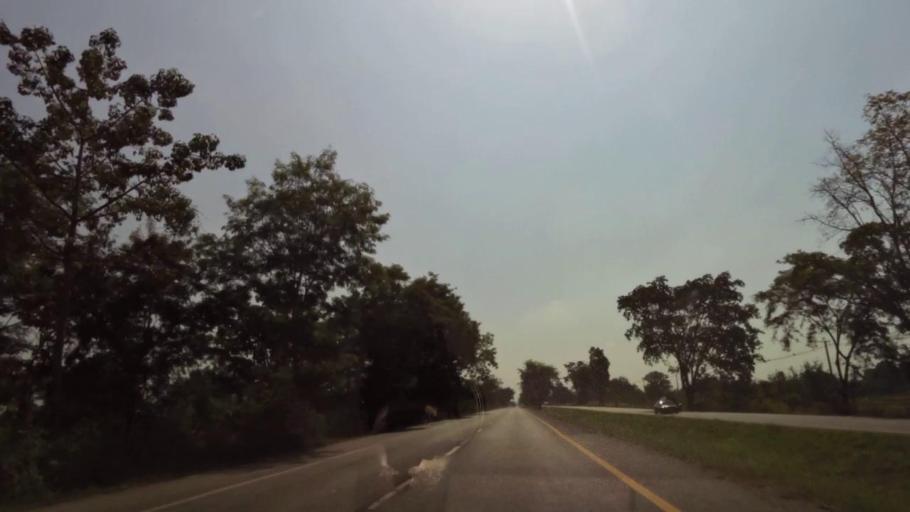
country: TH
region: Phichit
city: Bueng Na Rang
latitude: 16.2830
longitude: 100.1274
